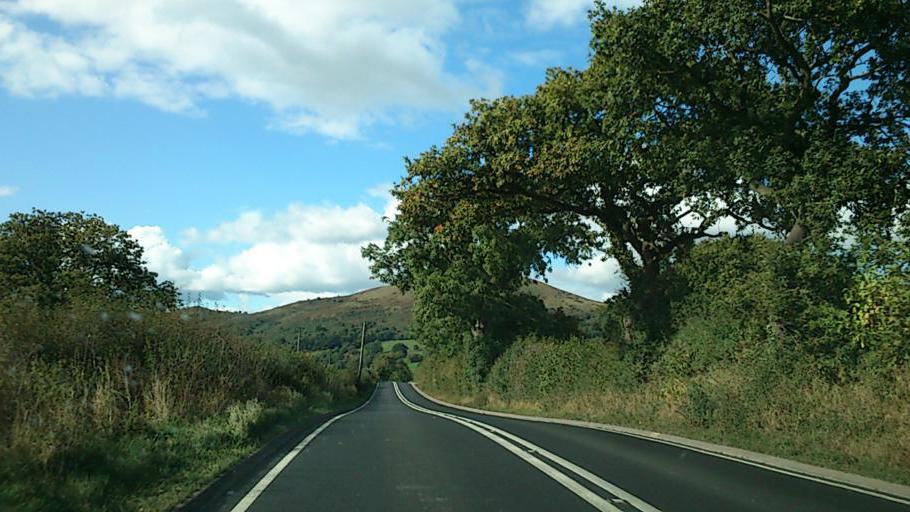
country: GB
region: England
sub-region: Shropshire
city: Westbury
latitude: 52.7052
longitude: -3.0067
